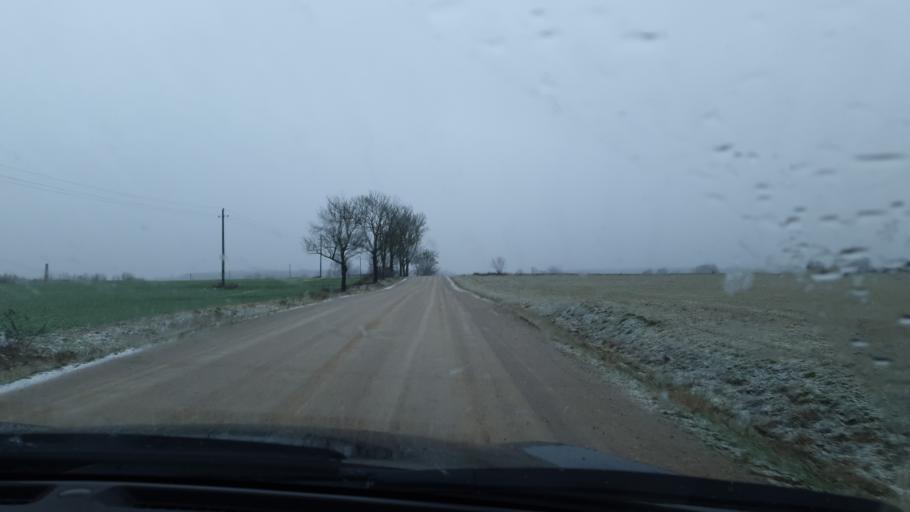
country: LT
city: Jieznas
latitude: 54.5810
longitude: 24.3166
